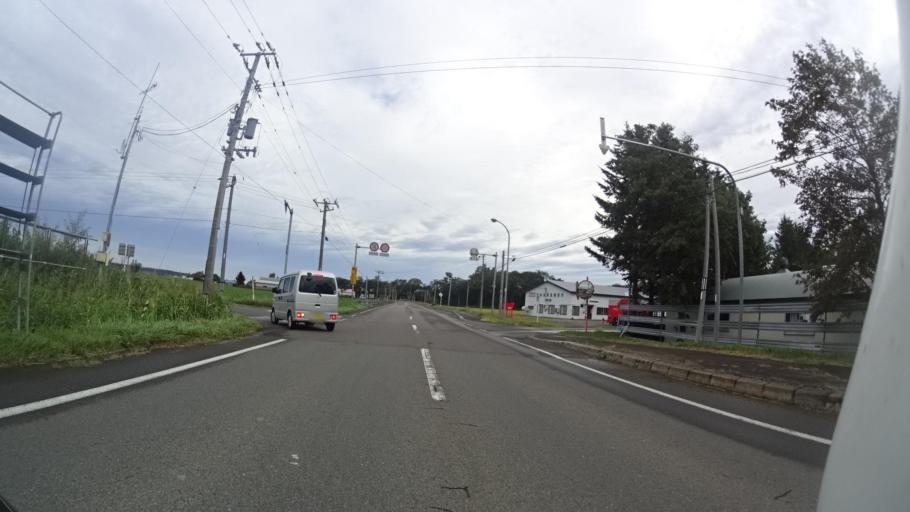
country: JP
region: Hokkaido
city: Abashiri
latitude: 43.8474
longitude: 144.5983
